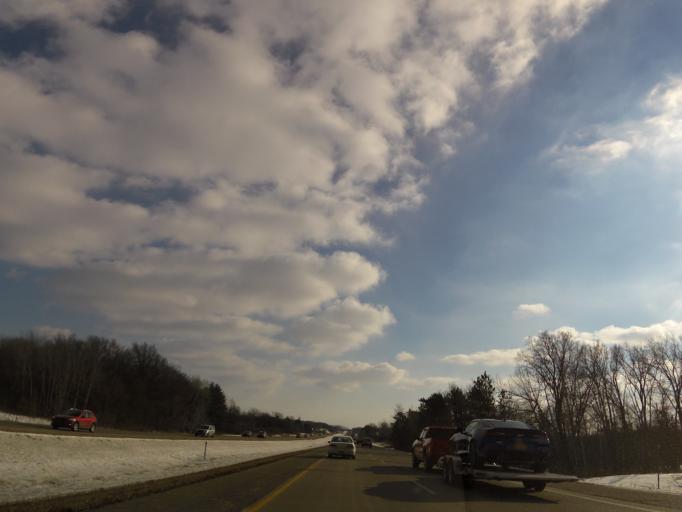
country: US
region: Wisconsin
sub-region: Juneau County
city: Mauston
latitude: 43.8191
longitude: -90.0799
